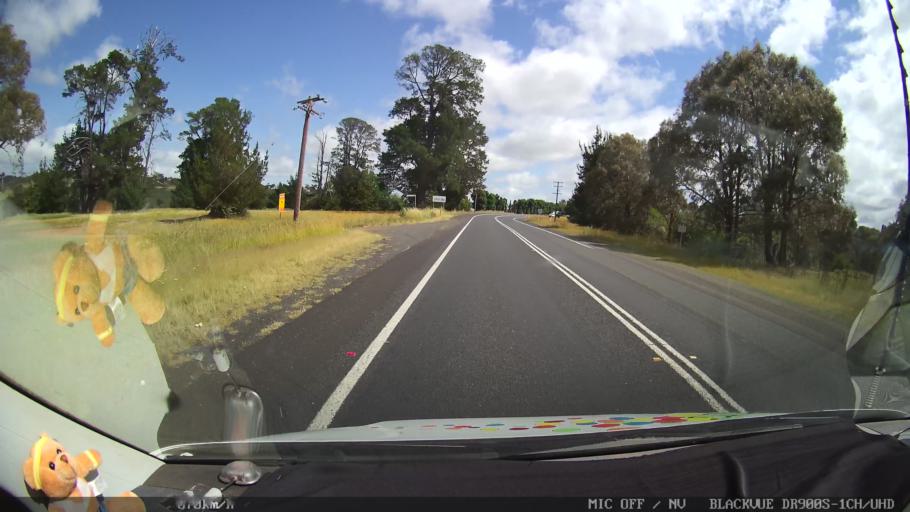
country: AU
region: New South Wales
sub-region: Glen Innes Severn
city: Glen Innes
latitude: -29.9315
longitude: 151.7237
